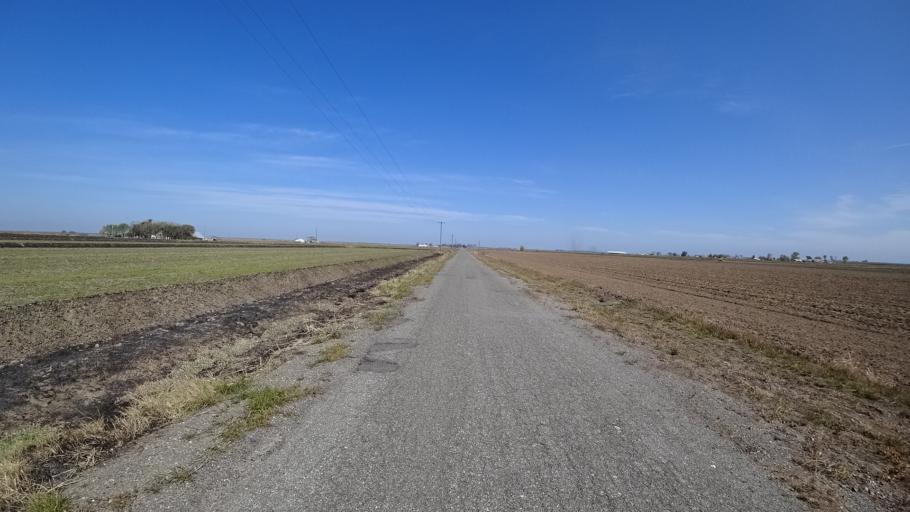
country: US
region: California
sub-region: Glenn County
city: Willows
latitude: 39.6068
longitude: -122.0744
